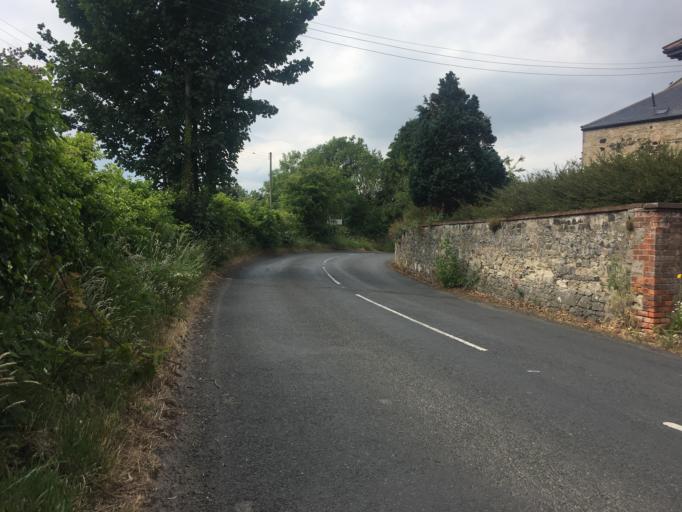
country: GB
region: England
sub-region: Northumberland
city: Bamburgh
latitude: 55.6027
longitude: -1.7676
